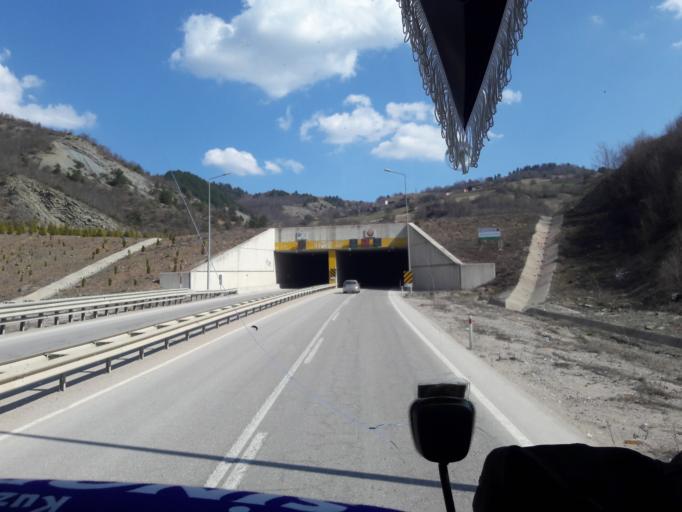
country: TR
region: Sinop
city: Erfelek
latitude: 41.6751
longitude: 34.9149
